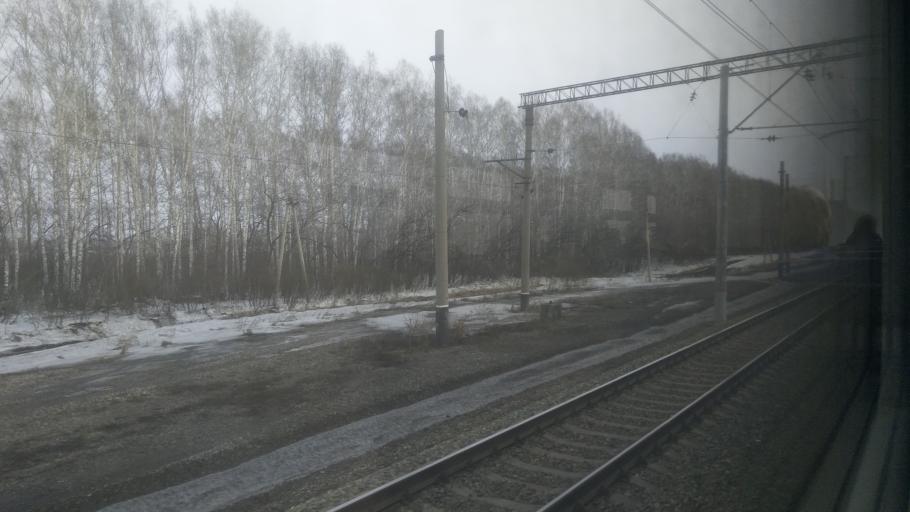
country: RU
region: Novosibirsk
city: Bolotnoye
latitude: 55.6937
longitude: 84.5355
